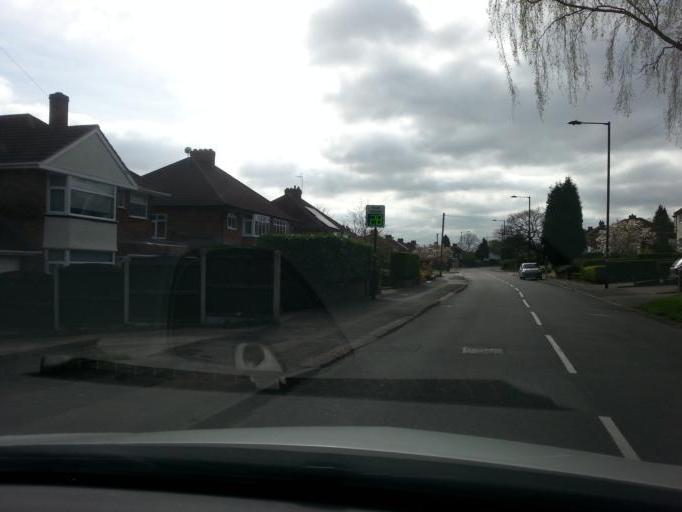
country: GB
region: England
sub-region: Staffordshire
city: Shenstone
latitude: 52.5973
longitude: -1.8460
